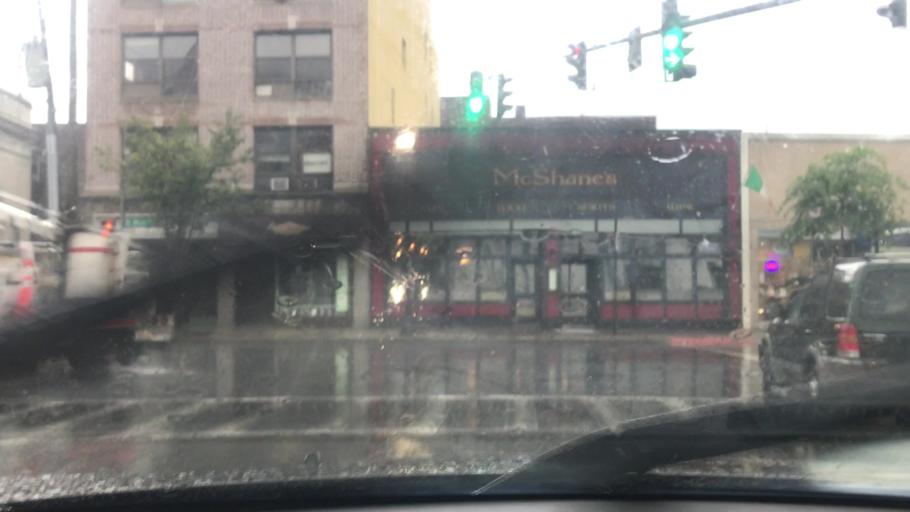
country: US
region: New York
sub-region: Westchester County
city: Port Chester
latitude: 41.0026
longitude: -73.6619
